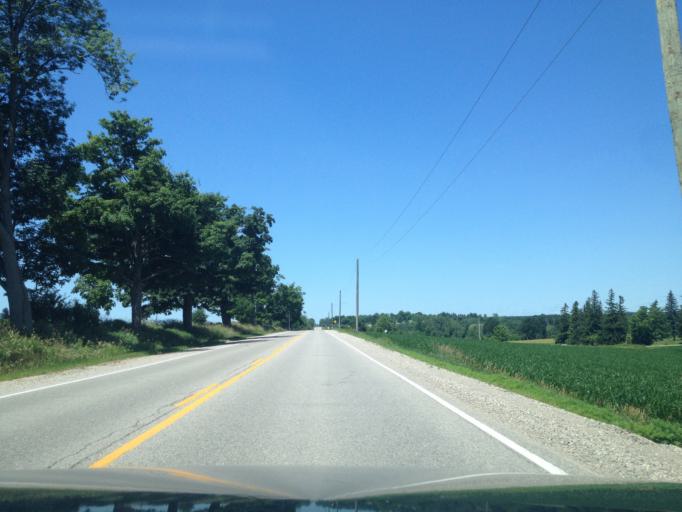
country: CA
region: Ontario
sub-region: Wellington County
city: Guelph
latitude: 43.6252
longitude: -80.2276
